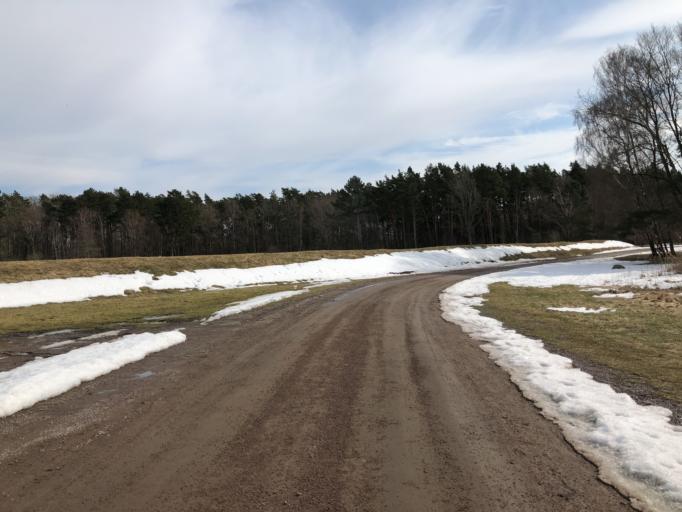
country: SE
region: Kalmar
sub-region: Kalmar Kommun
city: Kalmar
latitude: 56.6606
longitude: 16.3168
